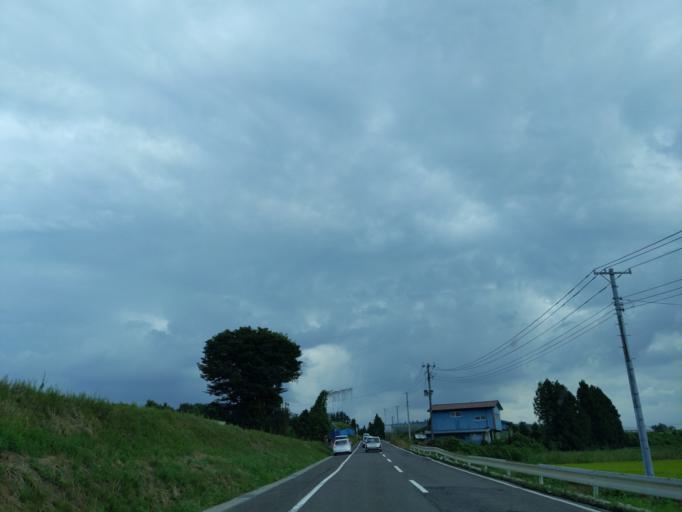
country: JP
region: Fukushima
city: Sukagawa
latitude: 37.3114
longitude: 140.3358
